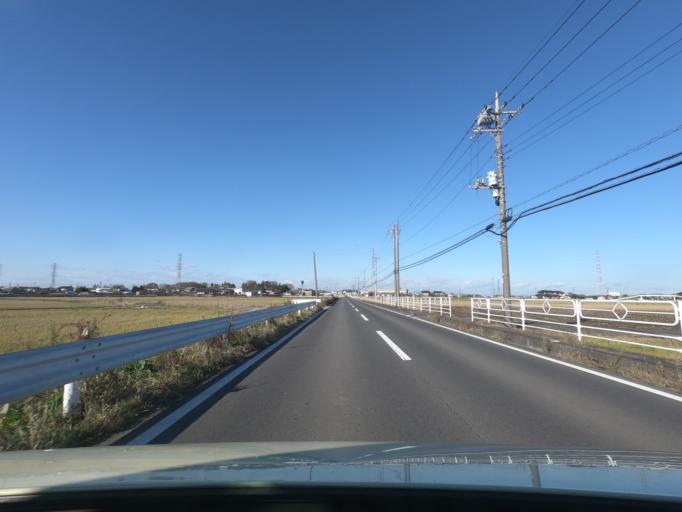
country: JP
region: Ibaraki
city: Ishige
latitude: 36.1687
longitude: 139.9890
